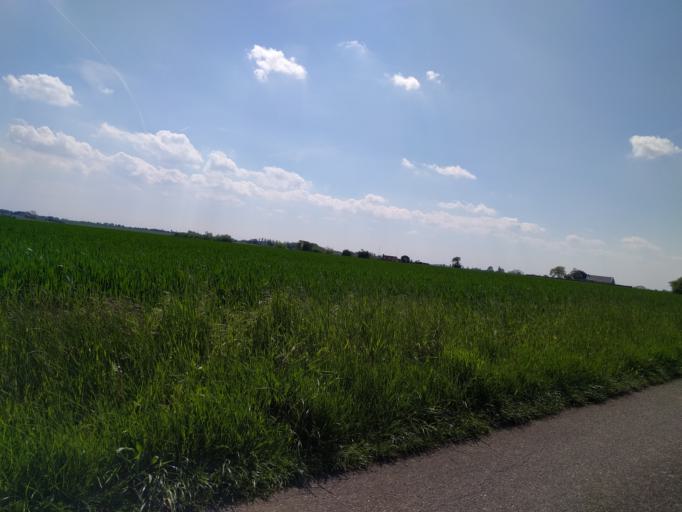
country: DK
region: Zealand
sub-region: Guldborgsund Kommune
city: Stubbekobing
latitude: 54.8882
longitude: 12.0889
